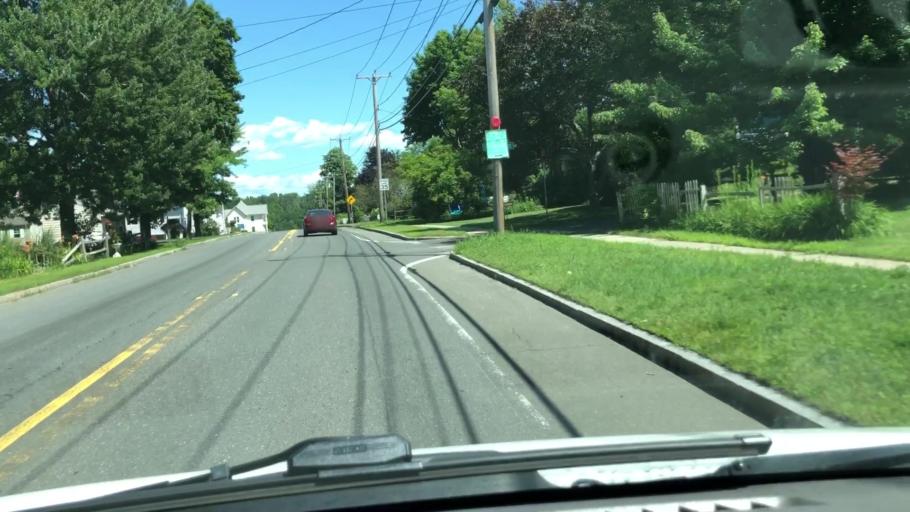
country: US
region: Massachusetts
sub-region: Hampshire County
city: Williamsburg
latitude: 42.3733
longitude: -72.6994
